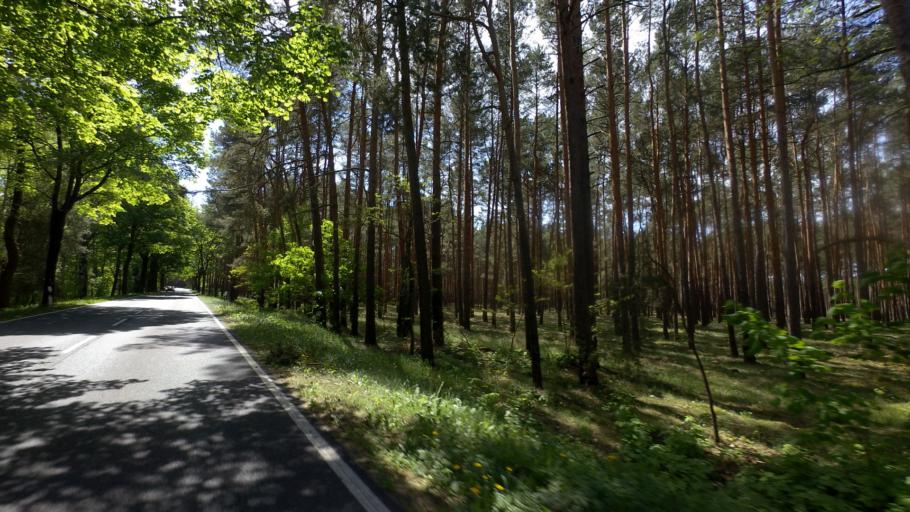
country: DE
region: Brandenburg
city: Luckenwalde
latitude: 52.1332
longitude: 13.1274
